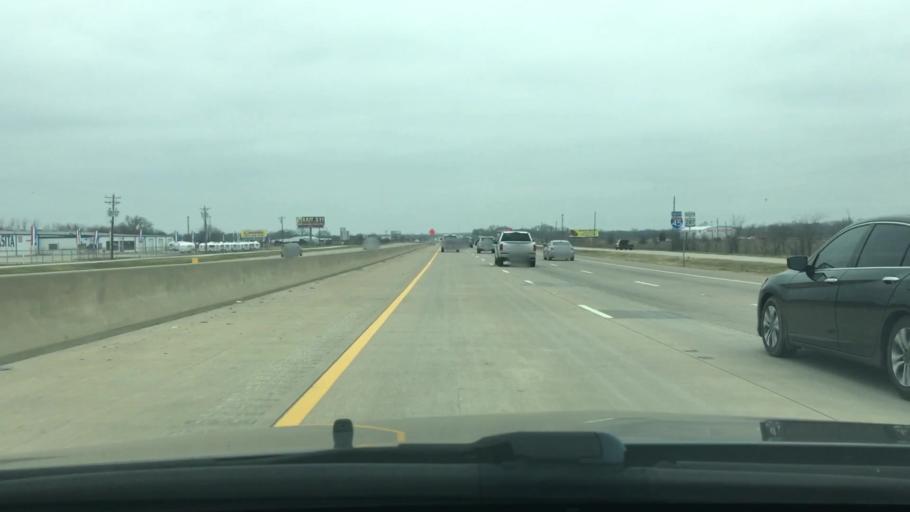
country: US
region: Texas
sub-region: Navarro County
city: Corsicana
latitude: 32.1921
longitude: -96.4729
